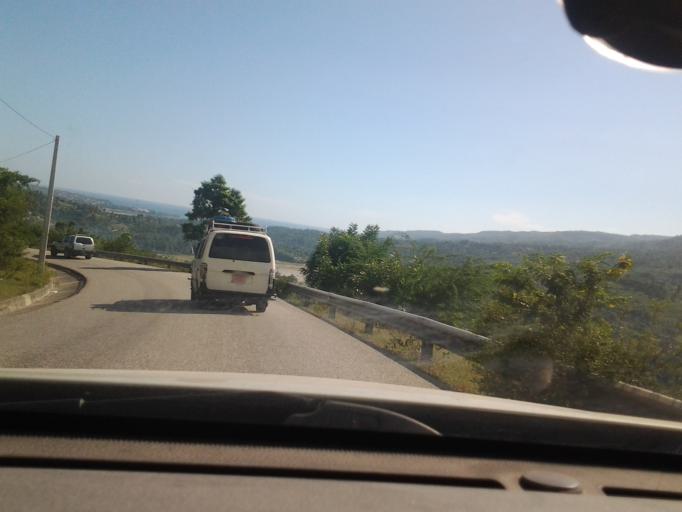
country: HT
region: Sud-Est
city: Jacmel
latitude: 18.2782
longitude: -72.5676
